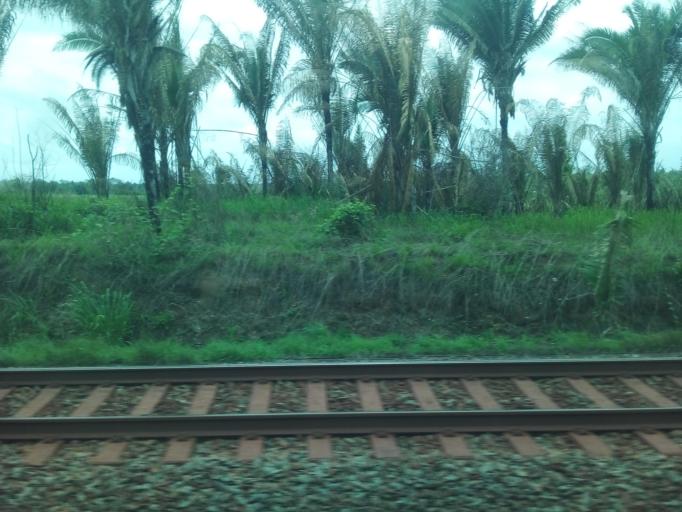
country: BR
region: Maranhao
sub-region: Santa Ines
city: Santa Ines
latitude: -3.6794
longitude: -45.3273
